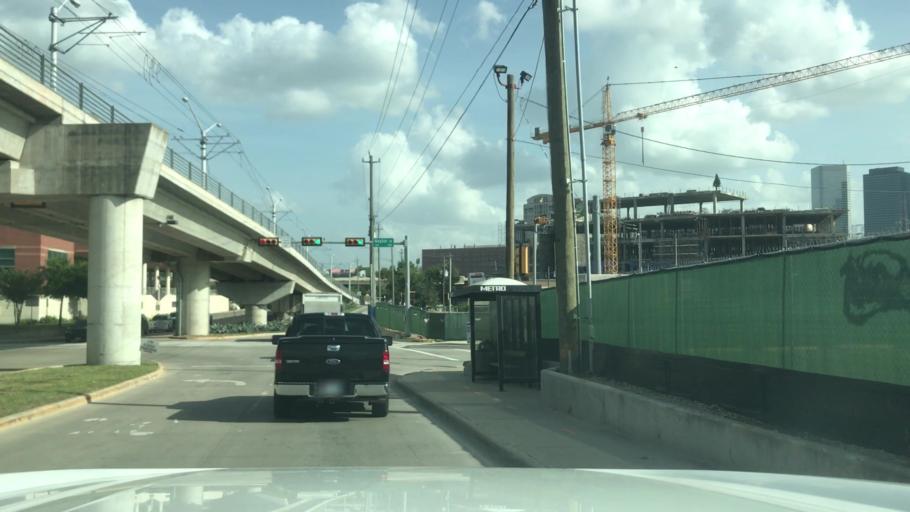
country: US
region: Texas
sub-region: Harris County
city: Houston
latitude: 29.7702
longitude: -95.3588
